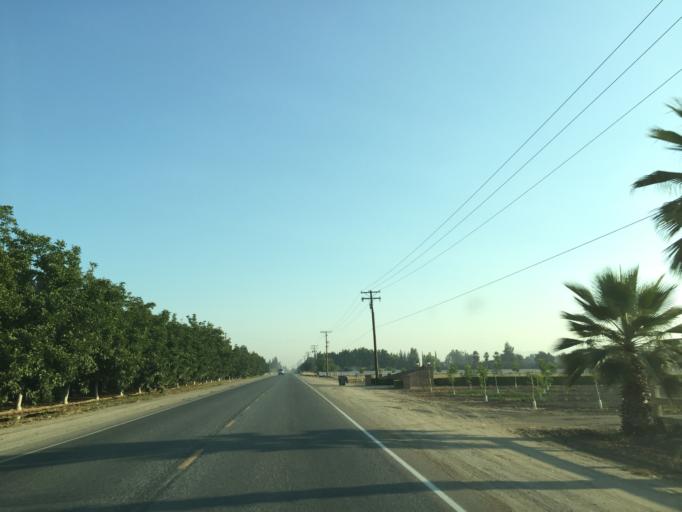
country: US
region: California
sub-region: Tulare County
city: Visalia
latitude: 36.3753
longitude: -119.2788
